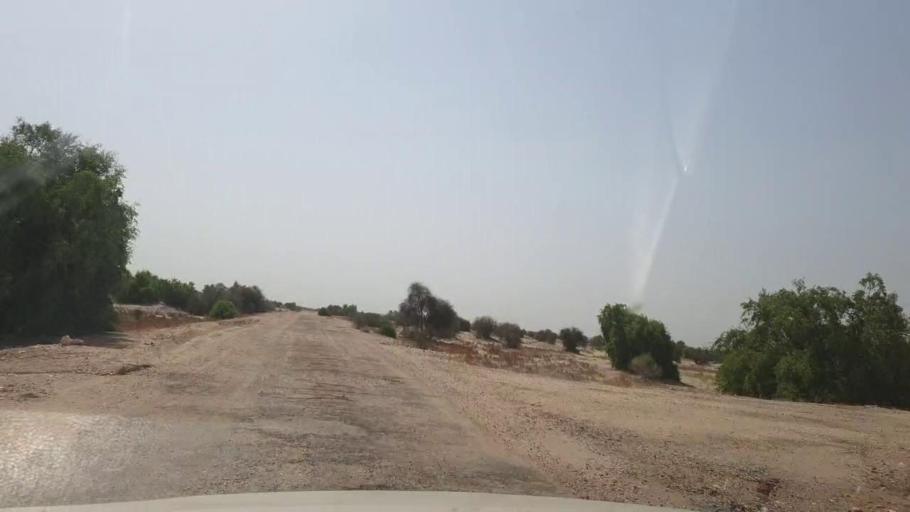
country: PK
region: Sindh
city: Rohri
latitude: 27.4500
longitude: 69.2302
